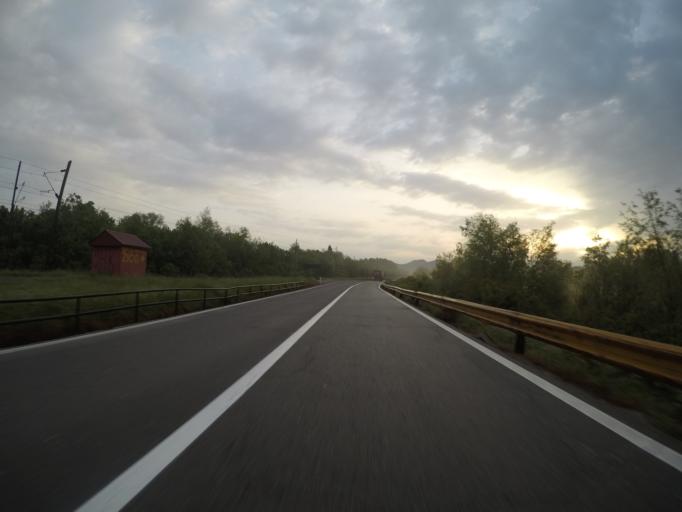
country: ME
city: Mojanovici
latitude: 42.2958
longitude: 19.1593
